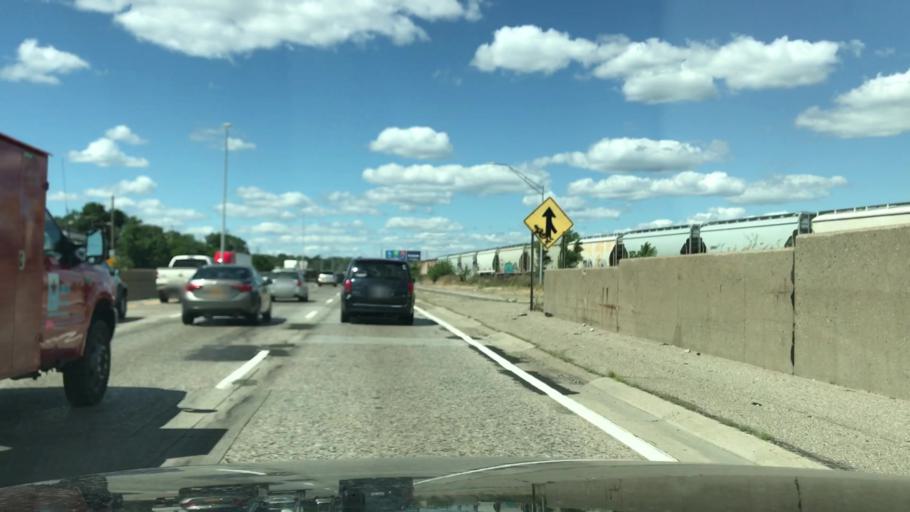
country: US
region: Michigan
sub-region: Kent County
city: Wyoming
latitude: 42.9291
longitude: -85.6814
